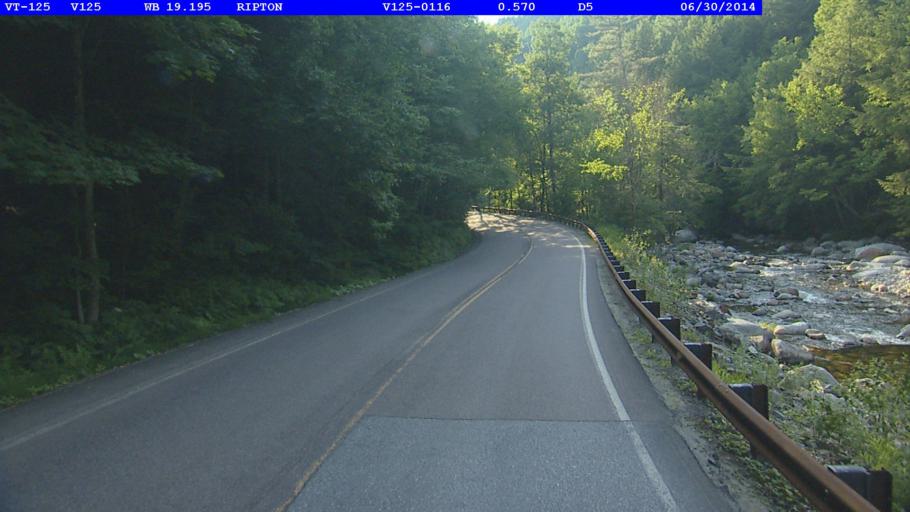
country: US
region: Vermont
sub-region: Addison County
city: Middlebury (village)
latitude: 43.9741
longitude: -73.0495
